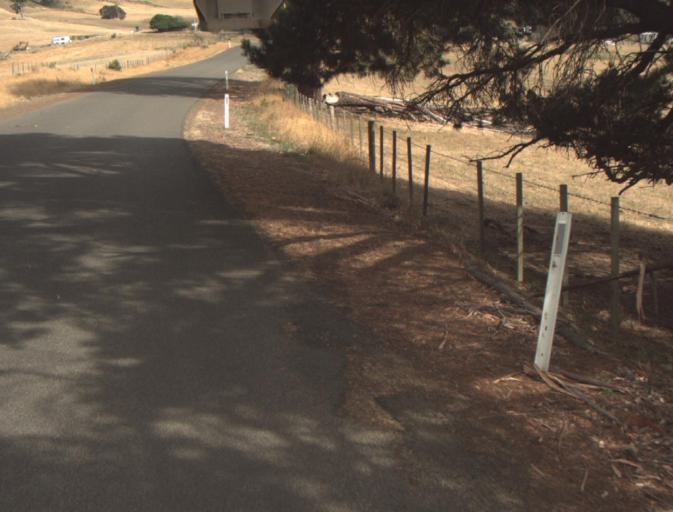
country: AU
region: Tasmania
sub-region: Dorset
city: Scottsdale
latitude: -41.4539
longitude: 147.5953
